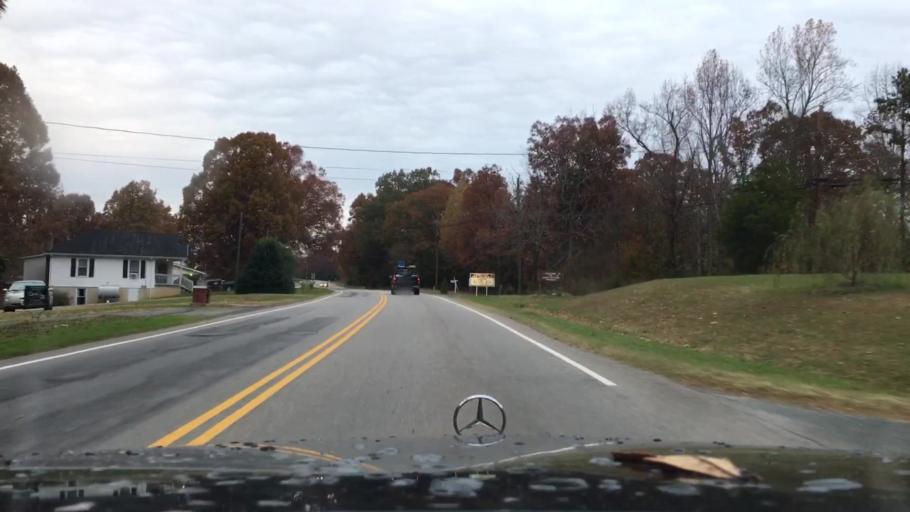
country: US
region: Virginia
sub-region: Campbell County
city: Altavista
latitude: 37.1321
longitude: -79.3068
